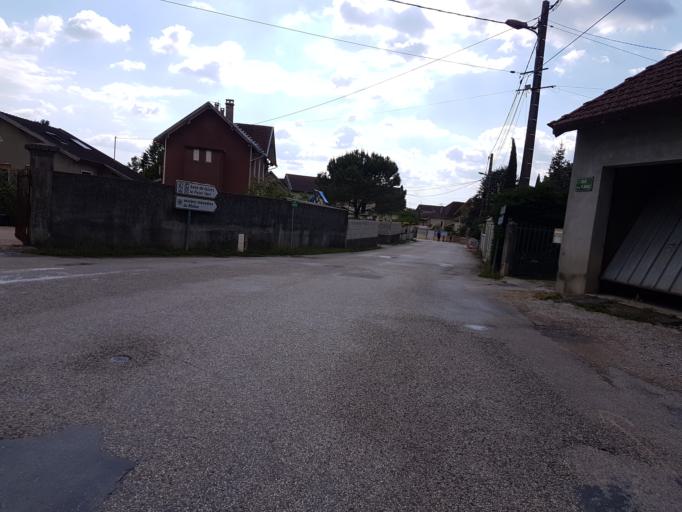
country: FR
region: Rhone-Alpes
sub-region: Departement de l'Isere
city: Bouvesse-Quirieu
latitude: 45.8078
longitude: 5.4478
